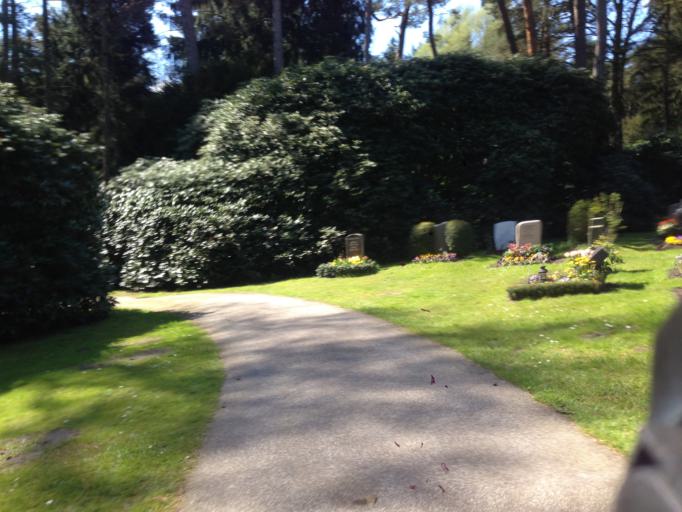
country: DE
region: Hamburg
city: Ohlsdorf
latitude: 53.6262
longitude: 10.0422
